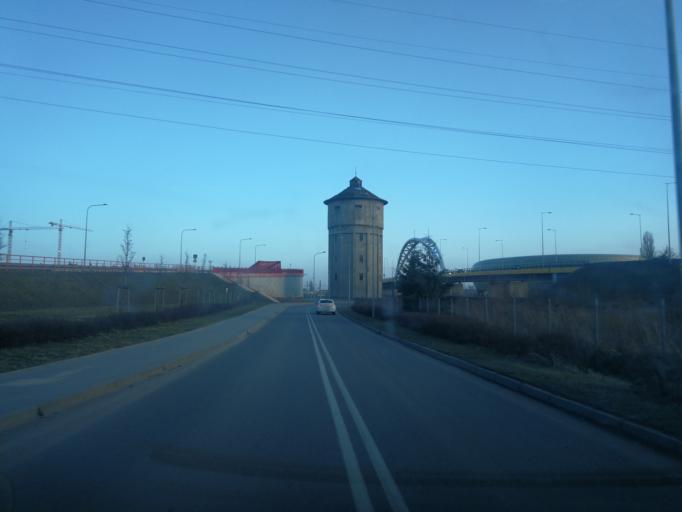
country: PL
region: Pomeranian Voivodeship
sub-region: Gdansk
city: Gdansk
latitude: 54.3957
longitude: 18.6362
